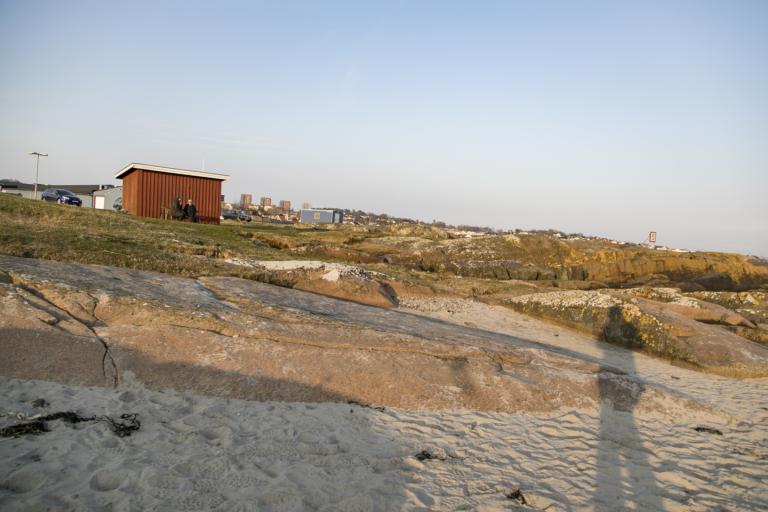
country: SE
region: Halland
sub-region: Varbergs Kommun
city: Varberg
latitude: 57.0840
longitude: 12.2491
